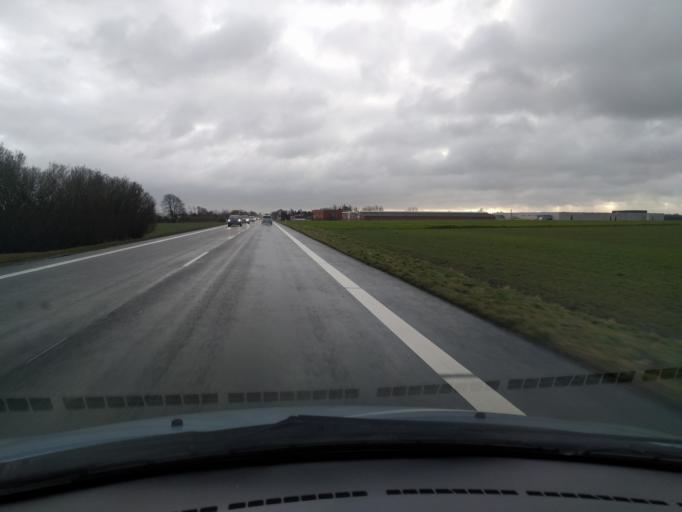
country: DK
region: South Denmark
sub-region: Kerteminde Kommune
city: Langeskov
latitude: 55.3778
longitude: 10.5501
